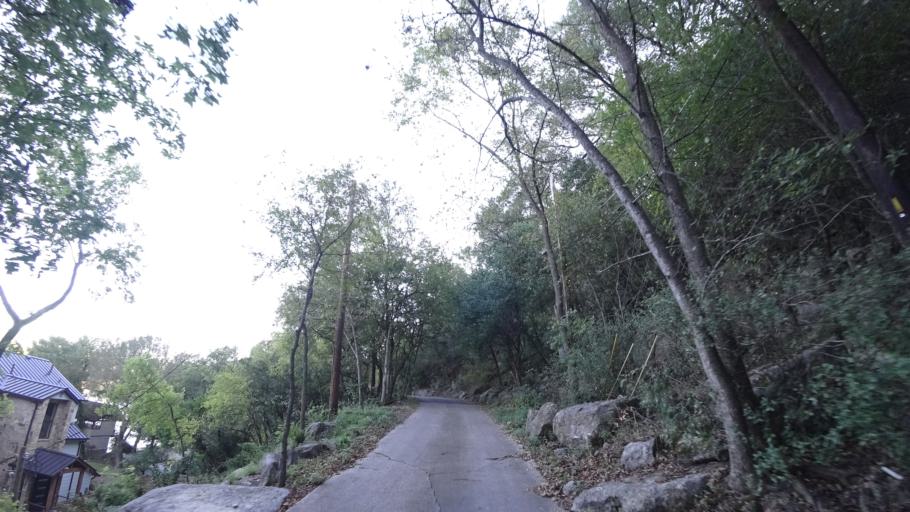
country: US
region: Texas
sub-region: Travis County
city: West Lake Hills
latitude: 30.3425
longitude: -97.8118
